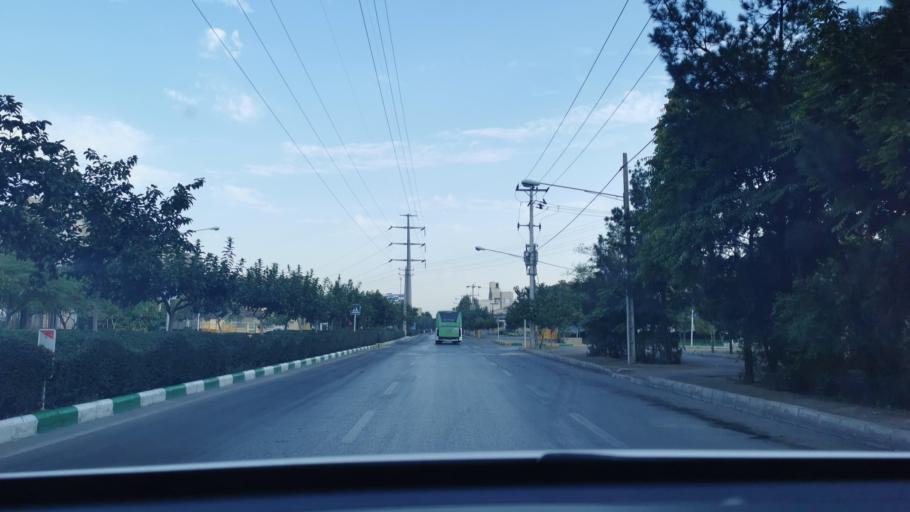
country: IR
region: Razavi Khorasan
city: Mashhad
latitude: 36.3538
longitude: 59.5281
